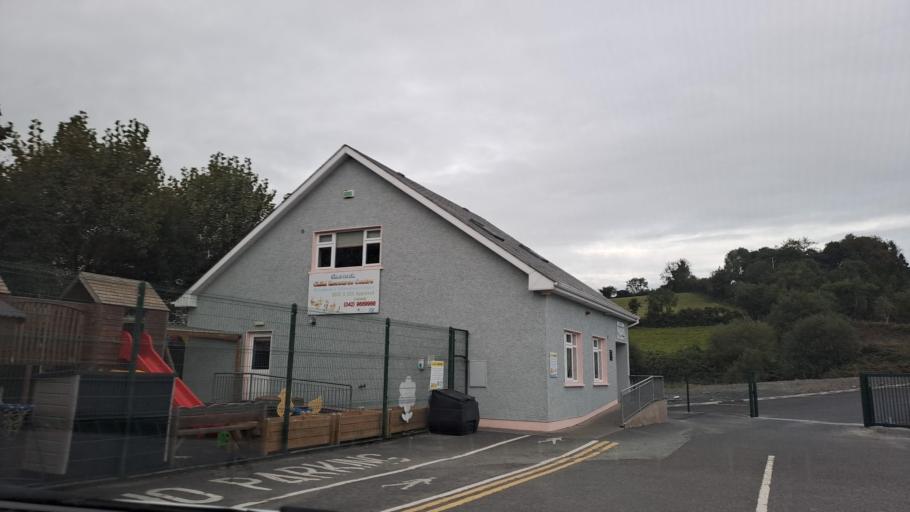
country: IE
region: Ulster
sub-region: An Cabhan
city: Bailieborough
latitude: 53.9930
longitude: -6.8936
